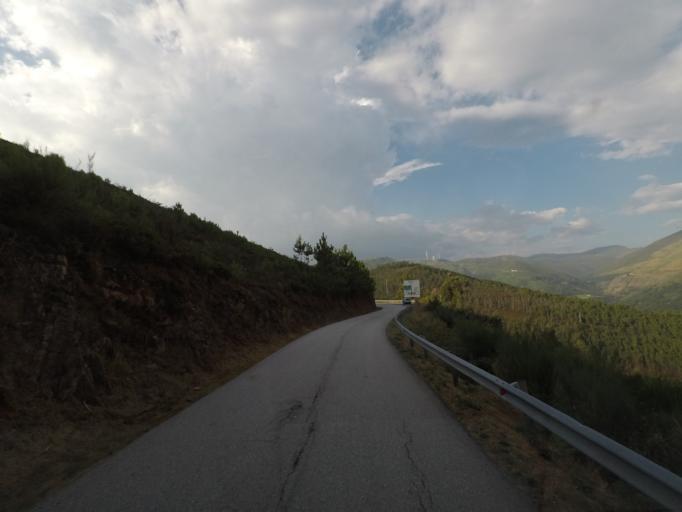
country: PT
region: Porto
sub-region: Baiao
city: Valadares
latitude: 41.1794
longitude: -7.9353
